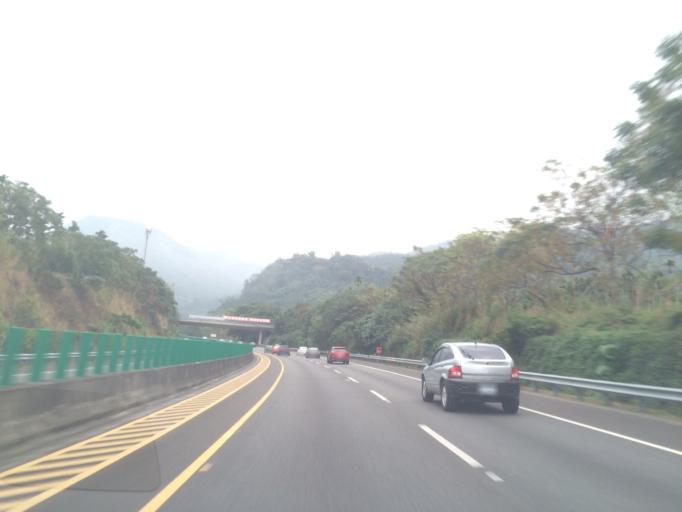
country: TW
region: Taiwan
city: Zhongxing New Village
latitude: 23.9871
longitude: 120.7908
